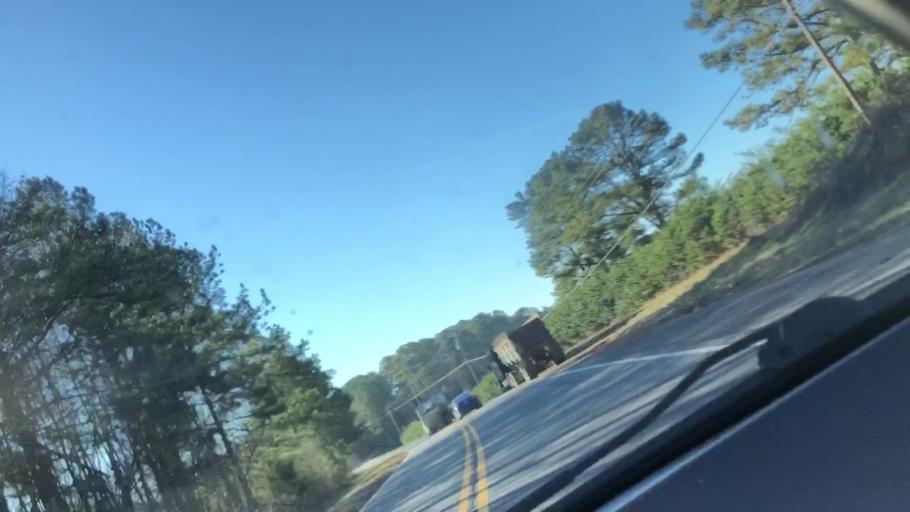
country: US
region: Georgia
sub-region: Bartow County
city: Cartersville
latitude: 34.2187
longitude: -84.8018
